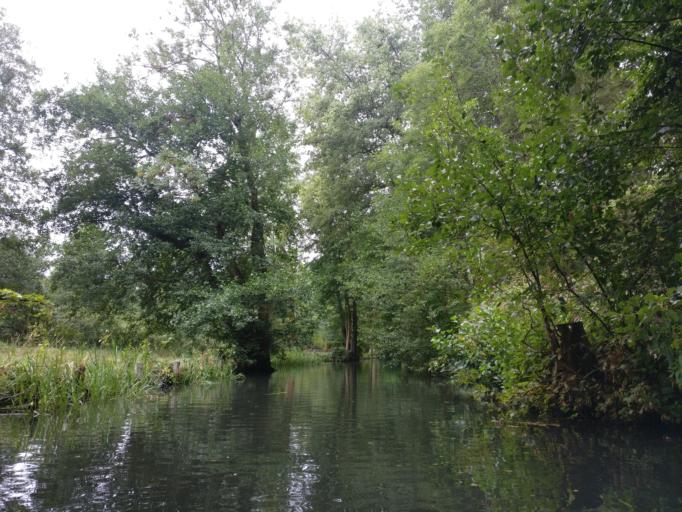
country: DE
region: Brandenburg
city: Lubbenau
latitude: 51.8681
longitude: 13.9950
